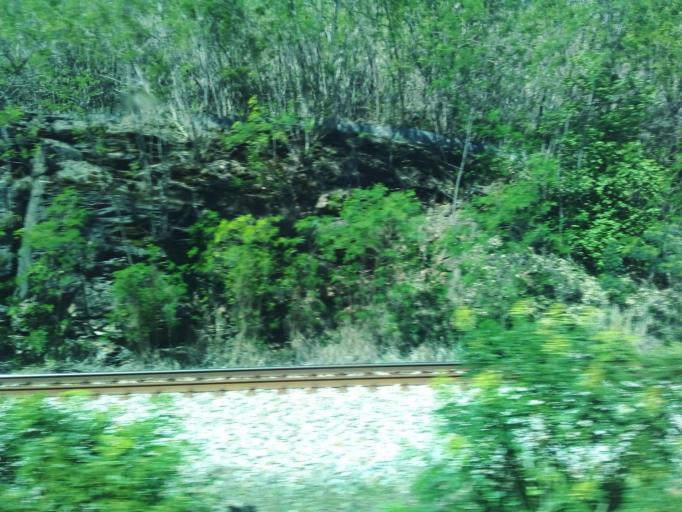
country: BR
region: Minas Gerais
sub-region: Governador Valadares
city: Governador Valadares
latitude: -18.8491
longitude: -41.8611
